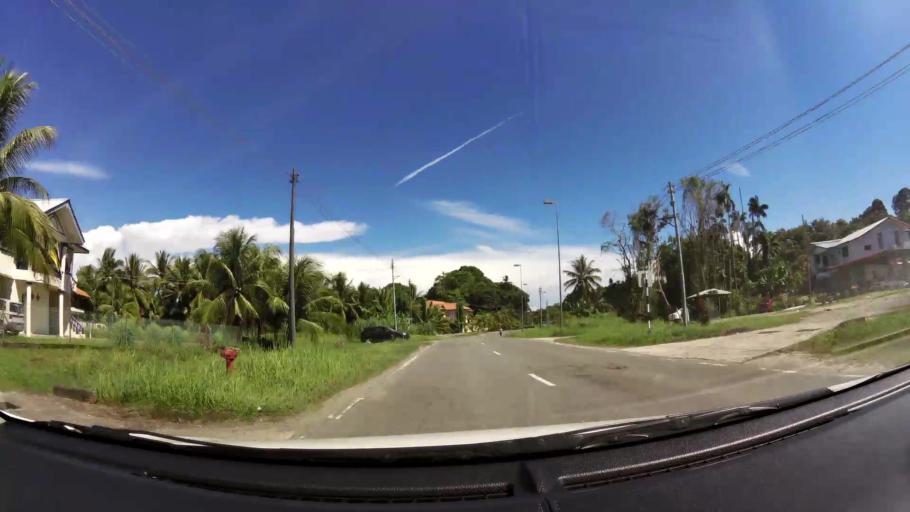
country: BN
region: Brunei and Muara
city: Bandar Seri Begawan
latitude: 5.0133
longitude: 115.0585
